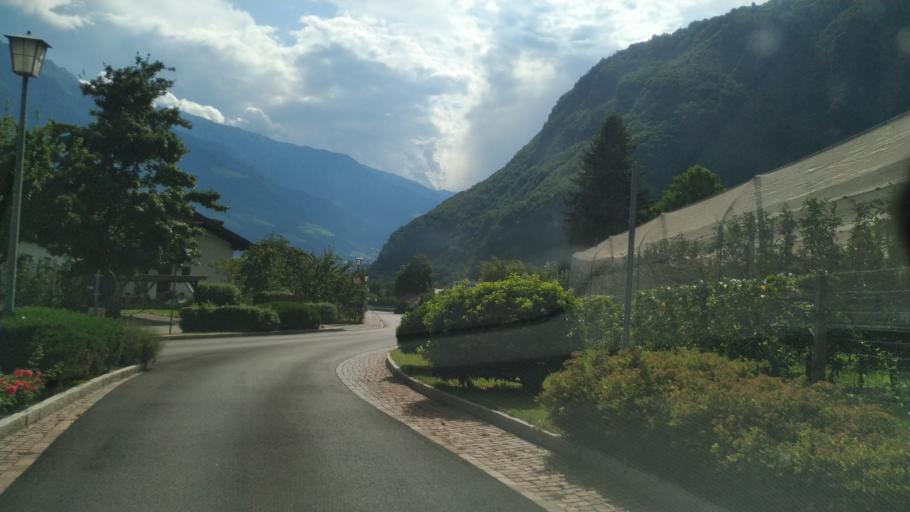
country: IT
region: Trentino-Alto Adige
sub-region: Bolzano
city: Rabla
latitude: 46.6758
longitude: 11.0606
